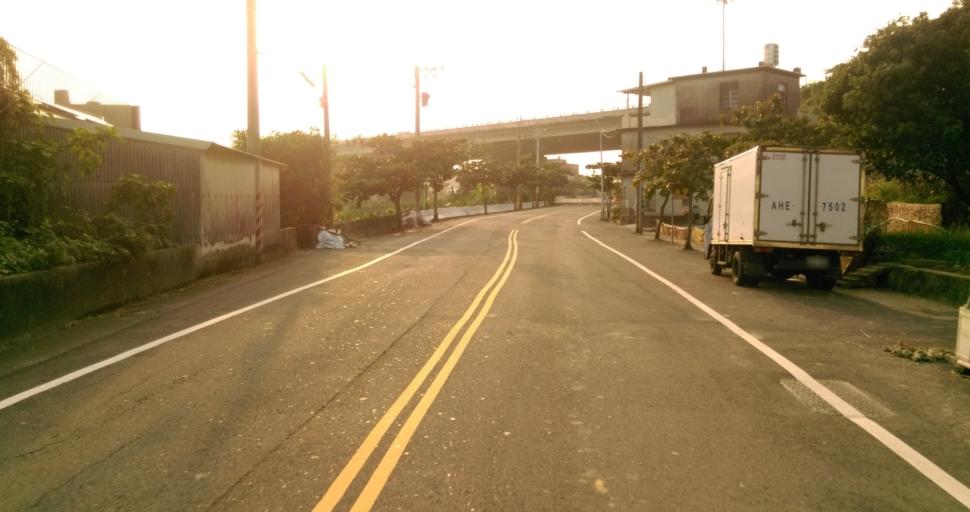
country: TW
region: Taiwan
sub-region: Hsinchu
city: Hsinchu
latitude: 24.7455
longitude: 120.9265
